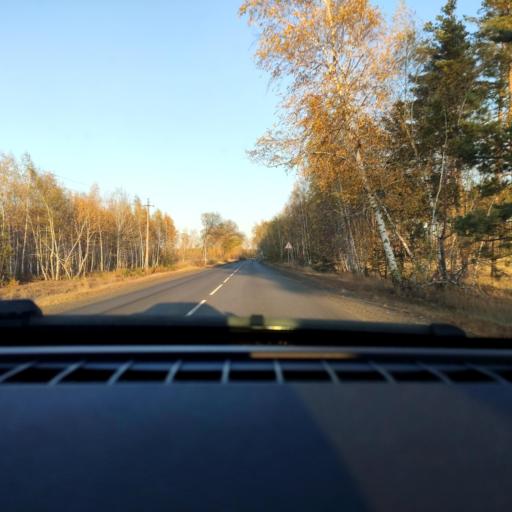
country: RU
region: Voronezj
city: Maslovka
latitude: 51.5806
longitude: 39.2765
